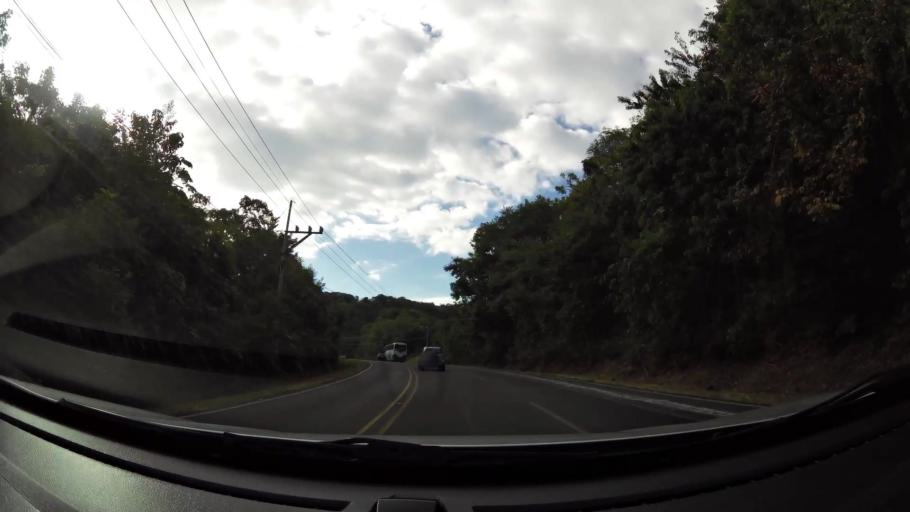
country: CR
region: Puntarenas
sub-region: Canton de Garabito
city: Jaco
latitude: 9.6814
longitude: -84.6487
